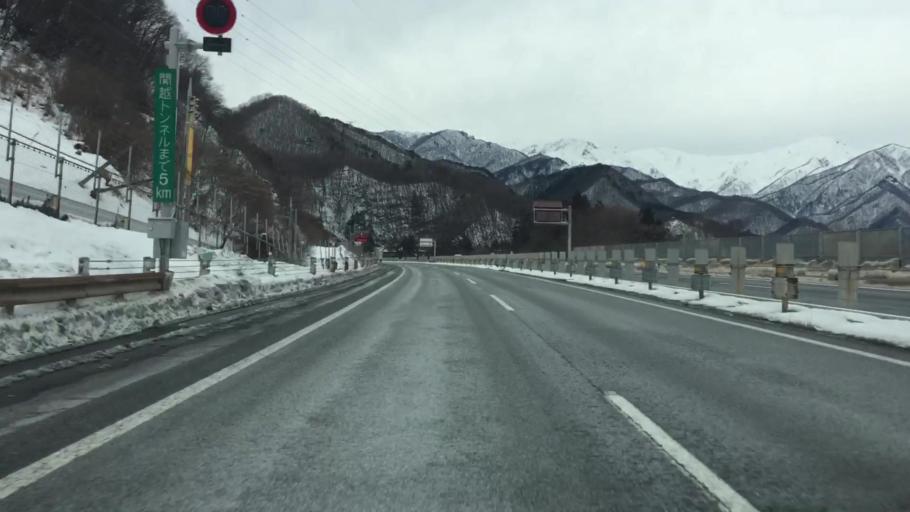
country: JP
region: Gunma
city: Numata
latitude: 36.7502
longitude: 138.9725
